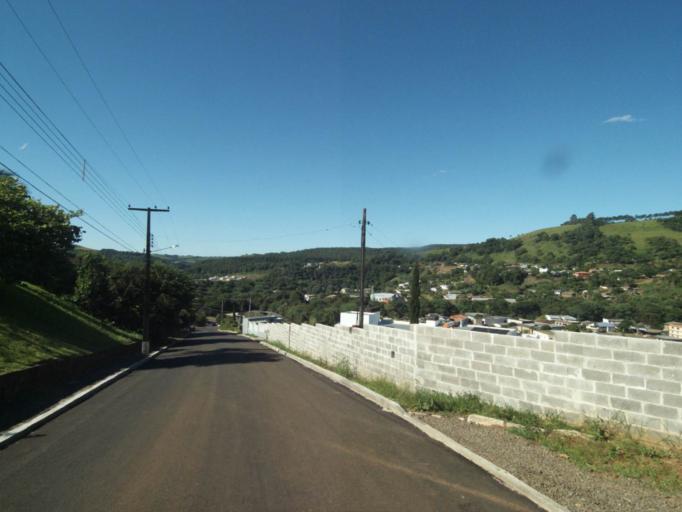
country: BR
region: Parana
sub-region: Ampere
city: Ampere
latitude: -26.1747
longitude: -53.3643
